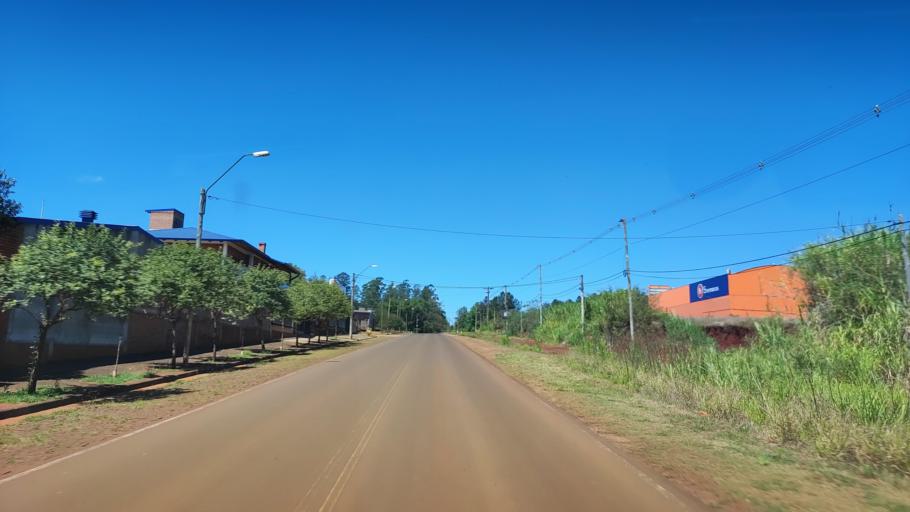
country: AR
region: Misiones
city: Puerto Rico
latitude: -26.8183
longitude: -55.0079
